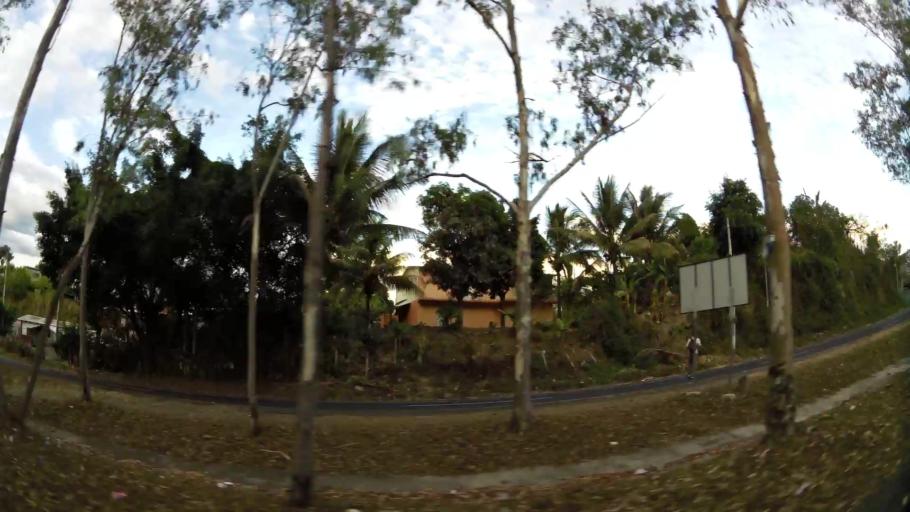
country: SV
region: San Vicente
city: San Sebastian
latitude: 13.6809
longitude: -88.8487
